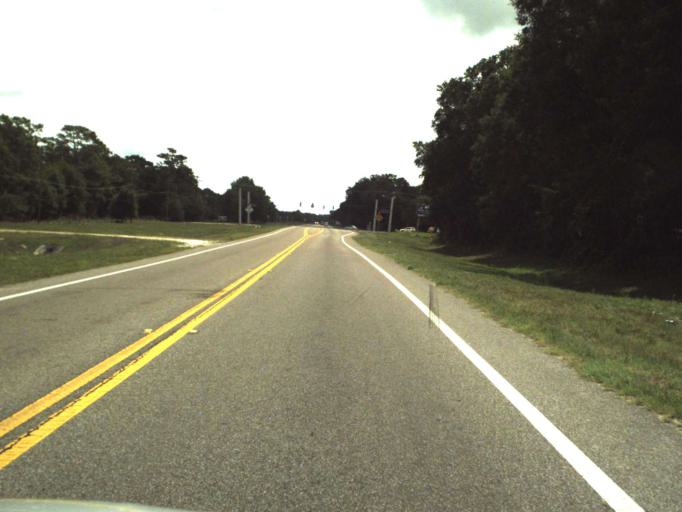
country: US
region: Florida
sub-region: Seminole County
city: Heathrow
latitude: 28.8146
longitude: -81.4087
